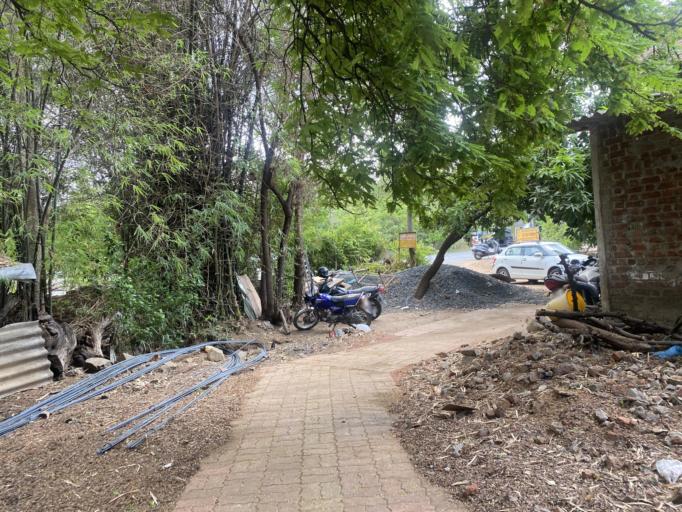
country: IN
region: Gujarat
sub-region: Valsad
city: Vapi
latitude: 20.3186
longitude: 72.8352
